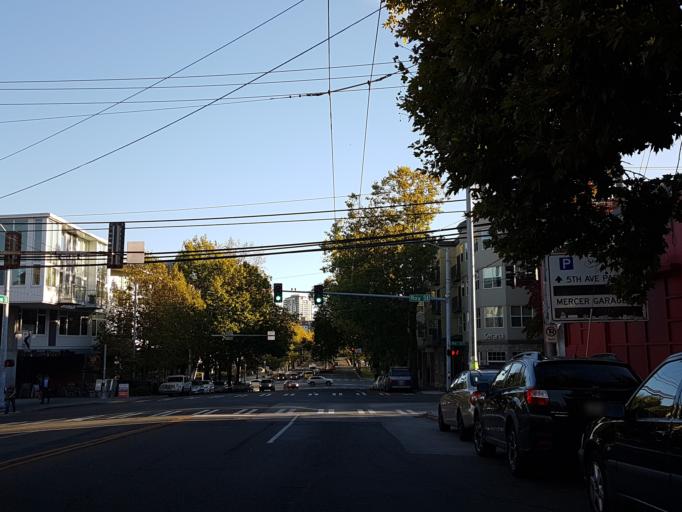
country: US
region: Washington
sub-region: King County
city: Seattle
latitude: 47.6258
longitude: -122.3476
